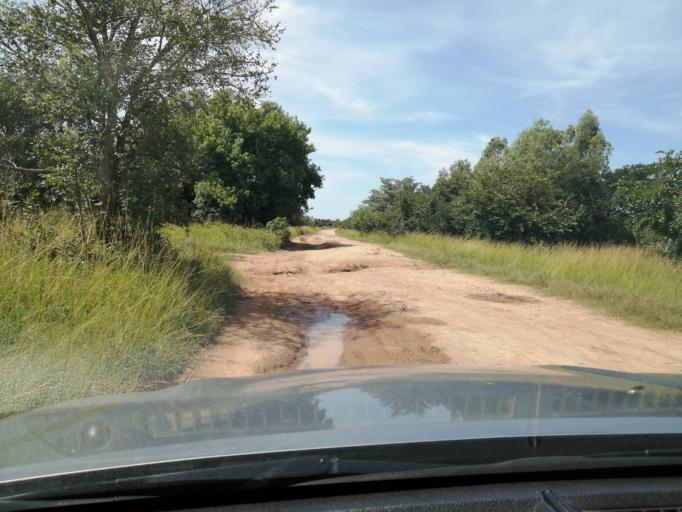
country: ZM
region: Central
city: Chibombo
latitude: -15.0093
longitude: 27.8280
